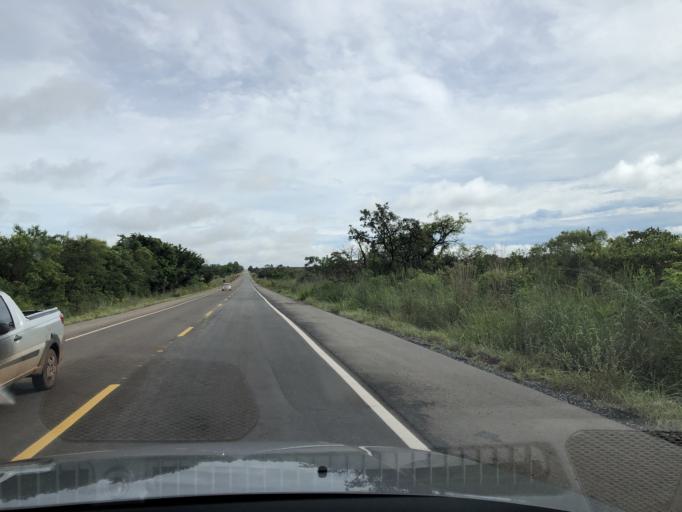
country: BR
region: Federal District
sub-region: Brasilia
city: Brasilia
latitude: -15.6661
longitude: -48.0864
